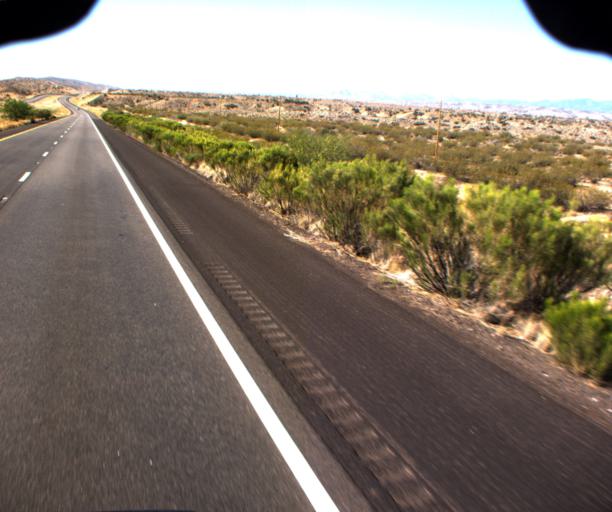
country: US
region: Arizona
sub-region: Mohave County
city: Kingman
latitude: 35.0228
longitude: -113.6648
